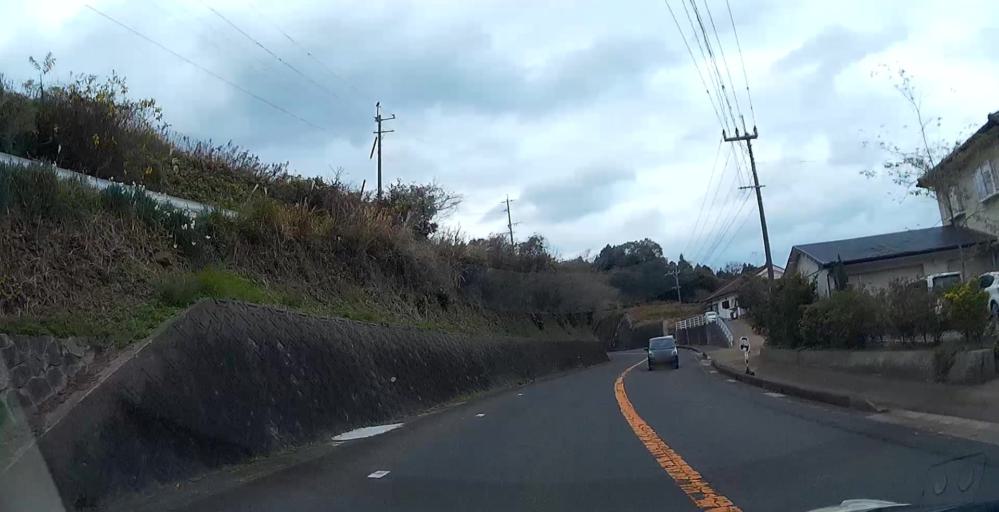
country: JP
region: Kagoshima
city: Akune
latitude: 32.1023
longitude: 130.1664
